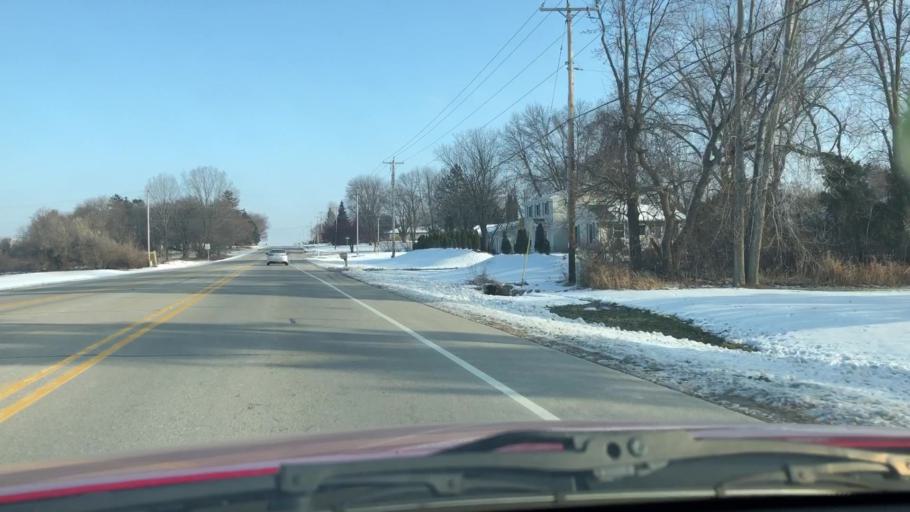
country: US
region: Wisconsin
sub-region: Outagamie County
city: Appleton
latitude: 44.3163
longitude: -88.4103
